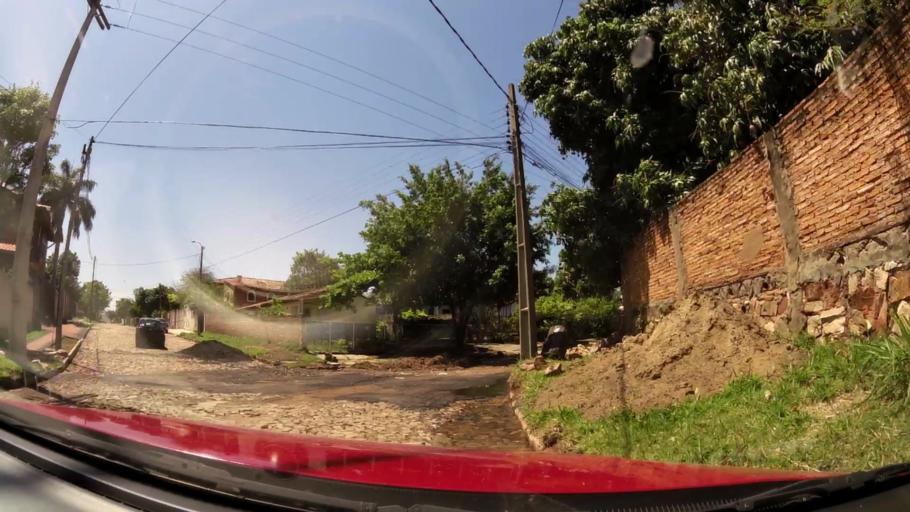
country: PY
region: Central
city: Colonia Mariano Roque Alonso
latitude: -25.2359
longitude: -57.5480
